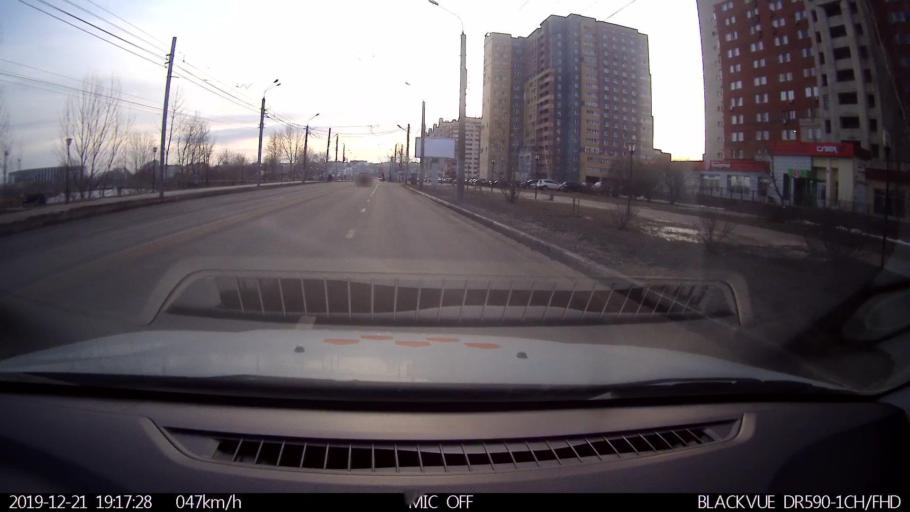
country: RU
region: Nizjnij Novgorod
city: Nizhniy Novgorod
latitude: 56.3367
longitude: 43.9397
